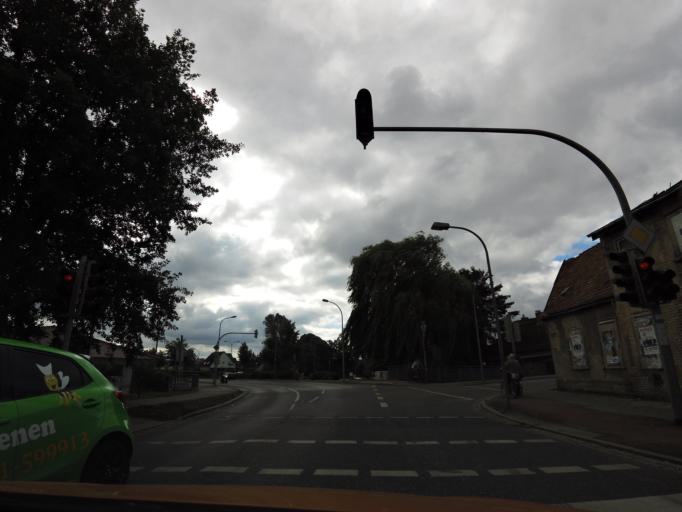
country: DE
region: Mecklenburg-Vorpommern
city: Guestrow
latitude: 53.7847
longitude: 12.1871
